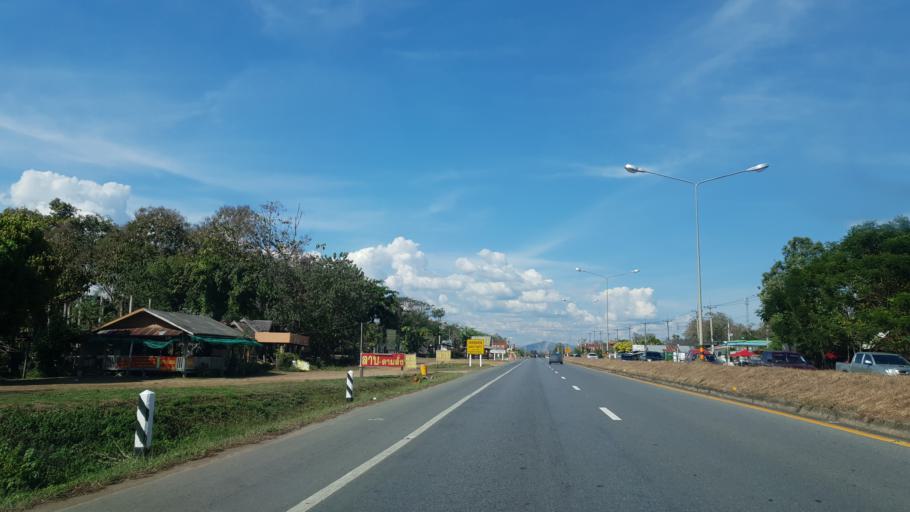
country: TH
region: Phrae
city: Den Chai
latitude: 17.9567
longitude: 100.0679
